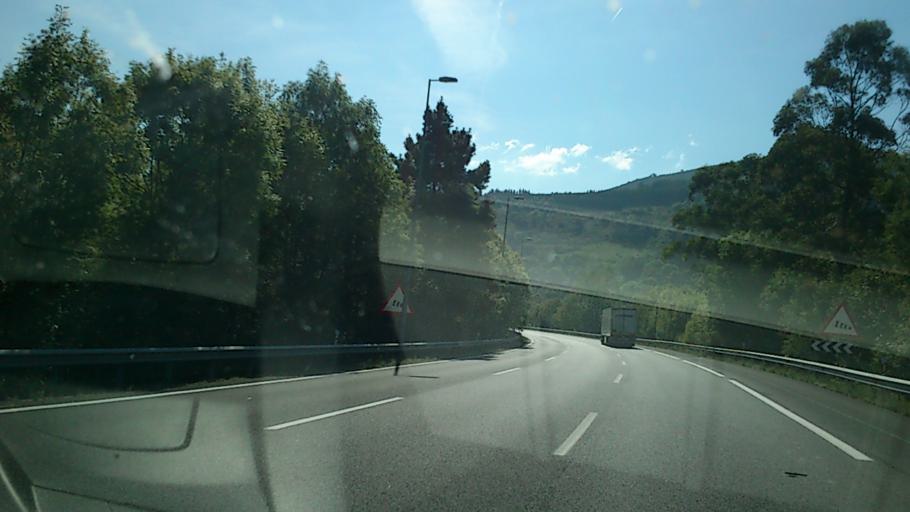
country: ES
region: Basque Country
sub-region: Bizkaia
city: Santutxu
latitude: 43.2280
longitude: -2.9155
